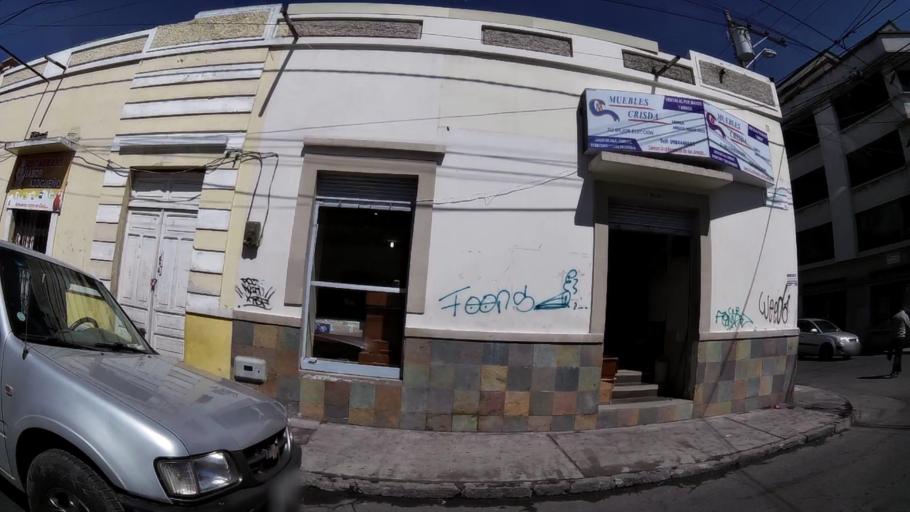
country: EC
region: Chimborazo
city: Riobamba
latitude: -1.6712
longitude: -78.6475
